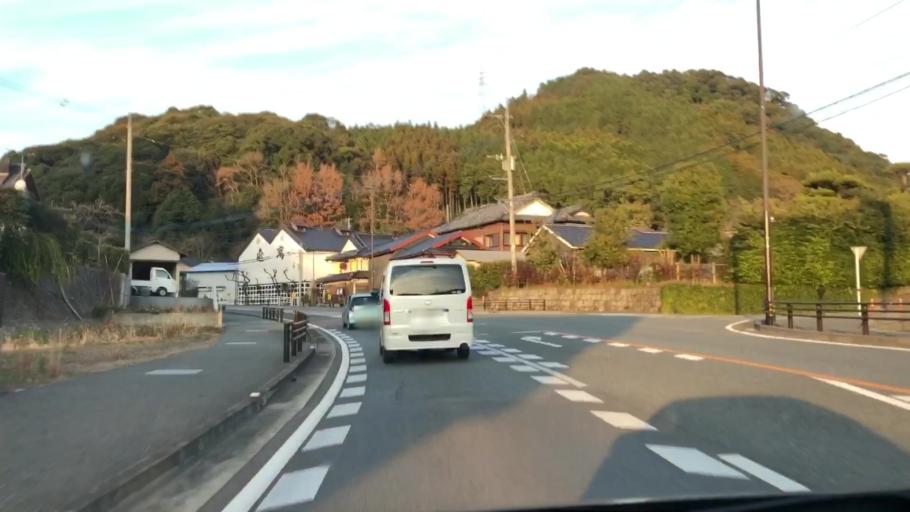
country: JP
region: Kumamoto
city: Minamata
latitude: 32.2344
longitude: 130.4651
